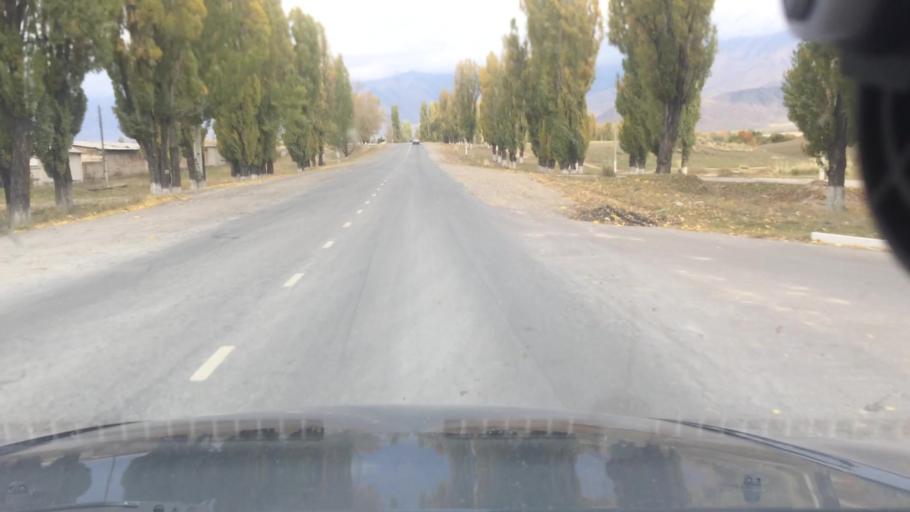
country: KG
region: Ysyk-Koel
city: Tyup
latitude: 42.7404
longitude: 78.3432
